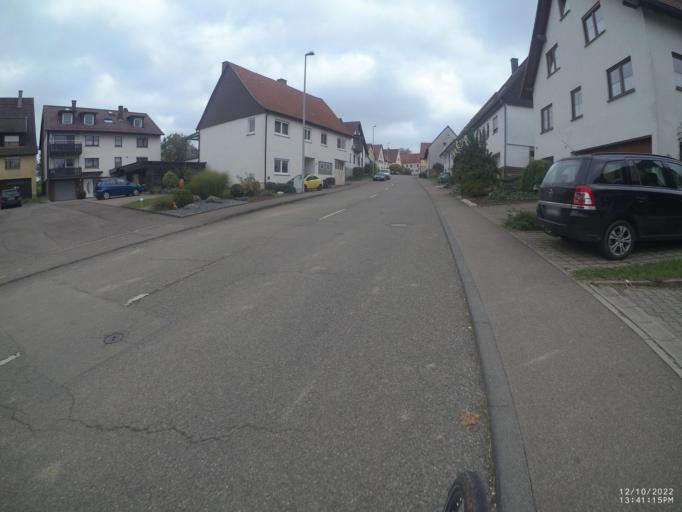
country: DE
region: Baden-Wuerttemberg
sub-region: Regierungsbezirk Stuttgart
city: Albershausen
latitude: 48.7094
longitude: 9.5491
